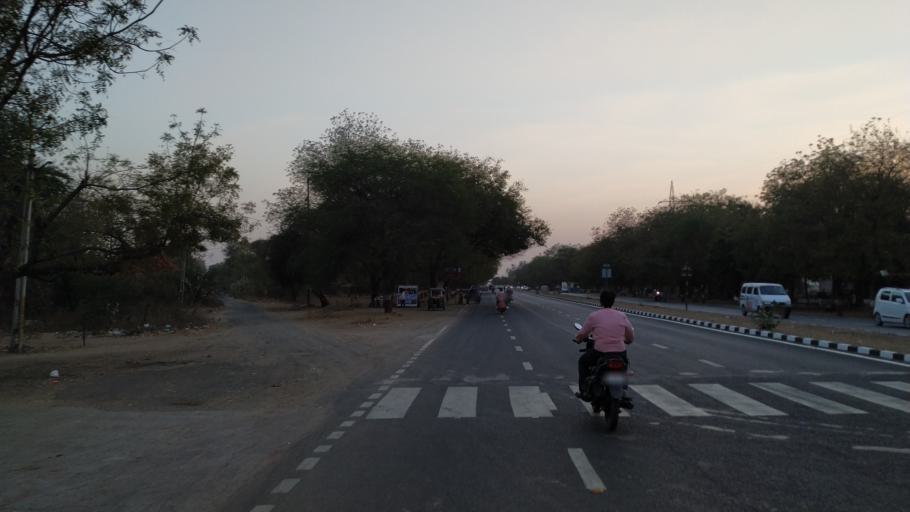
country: IN
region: Gujarat
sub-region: Gandhinagar
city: Adalaj
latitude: 23.1242
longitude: 72.6210
